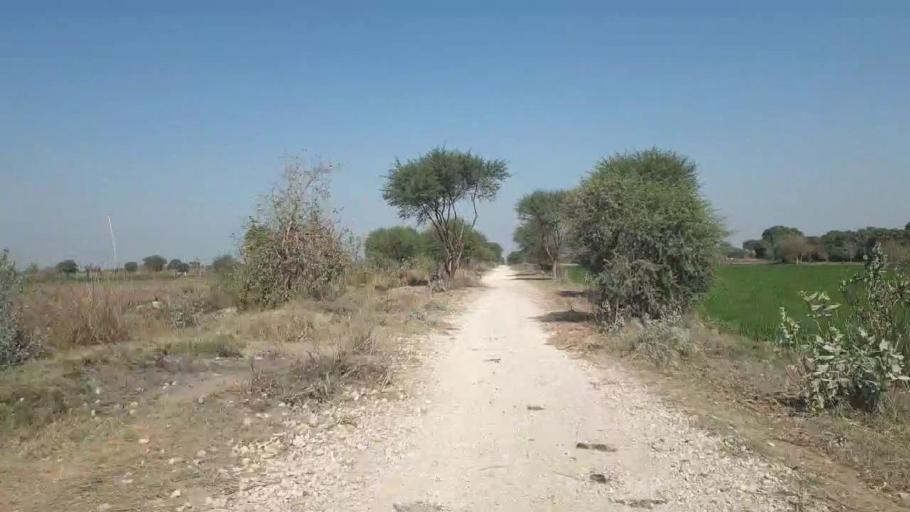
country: PK
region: Sindh
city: Chambar
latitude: 25.3068
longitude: 68.6956
